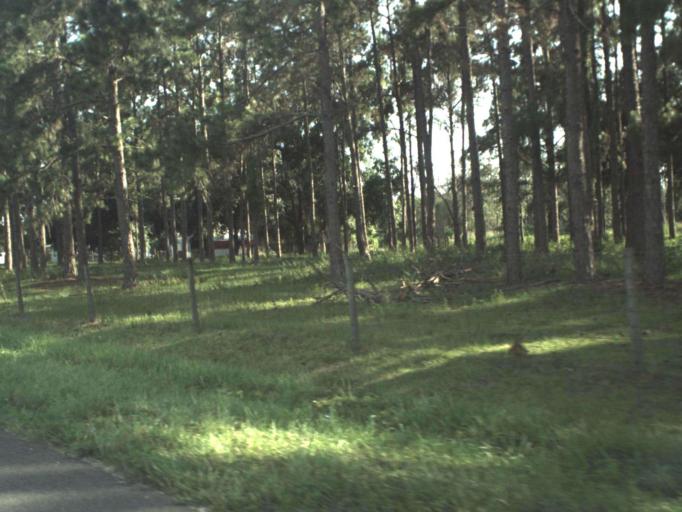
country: US
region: Florida
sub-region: Lake County
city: Groveland
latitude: 28.4877
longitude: -81.8367
